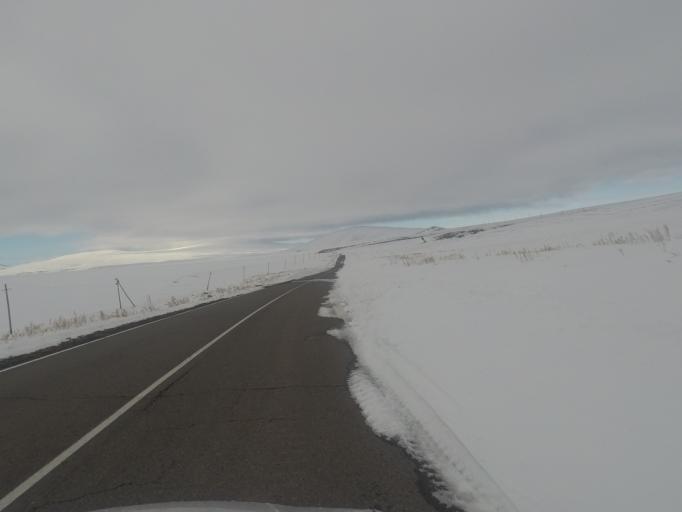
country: GE
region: Samtskhe-Javakheti
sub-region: Ninotsminda
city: Ninotsminda
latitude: 41.4227
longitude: 43.8336
